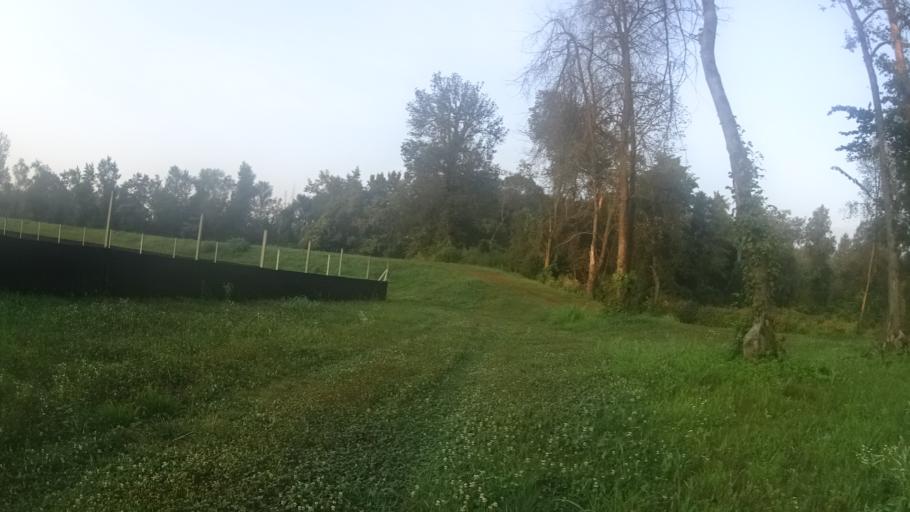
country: SI
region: Zavrc
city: Zavrc
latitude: 46.3925
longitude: 16.0514
